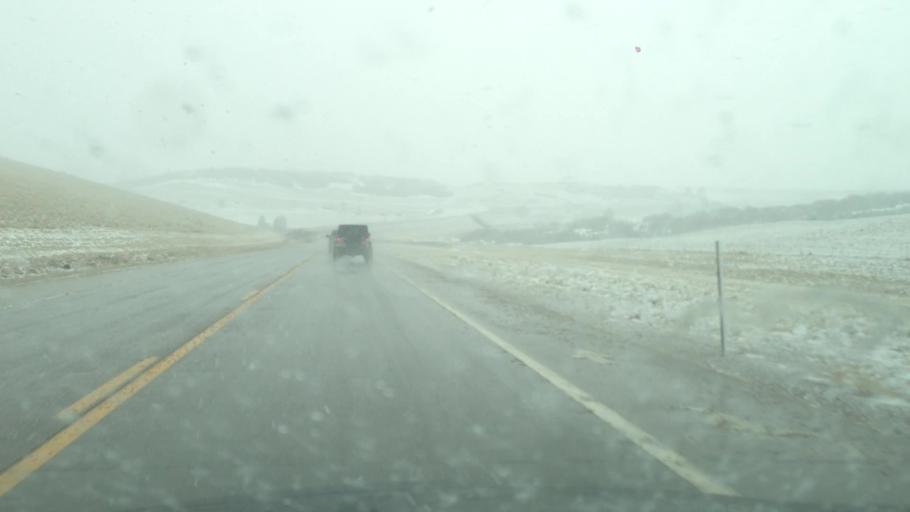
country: US
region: Colorado
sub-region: Park County
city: Castle Pines North
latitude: 39.4788
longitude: -104.8609
